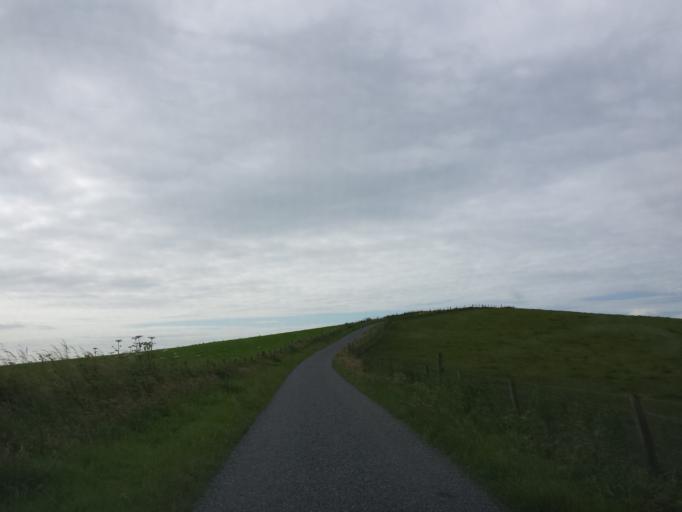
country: GB
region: Scotland
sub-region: Dumfries and Galloway
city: Stranraer
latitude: 54.8813
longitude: -5.1188
